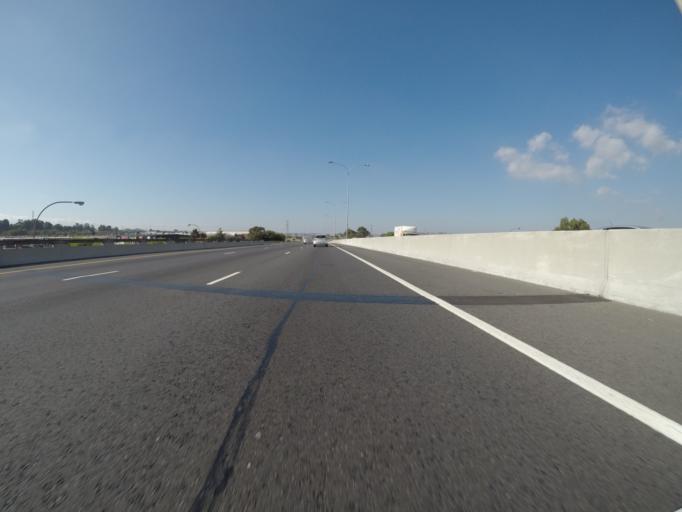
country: ZA
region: Western Cape
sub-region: City of Cape Town
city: Kraaifontein
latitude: -33.9144
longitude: 18.6684
